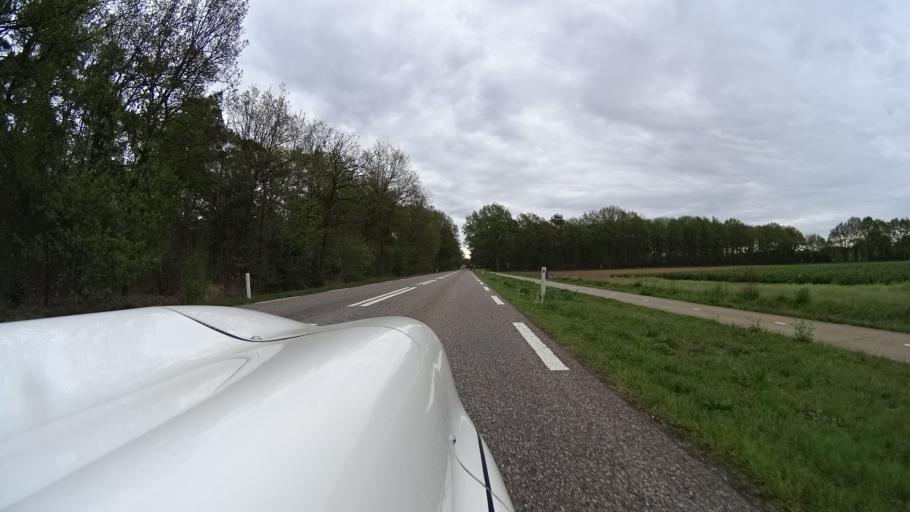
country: NL
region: North Brabant
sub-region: Gemeente Boxmeer
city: Overloon
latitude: 51.5400
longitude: 5.9134
